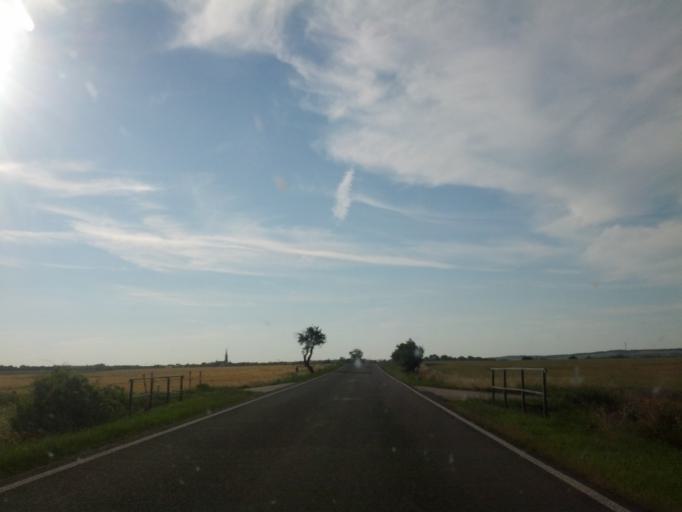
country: DE
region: Thuringia
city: Seebergen
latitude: 50.8828
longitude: 10.7982
